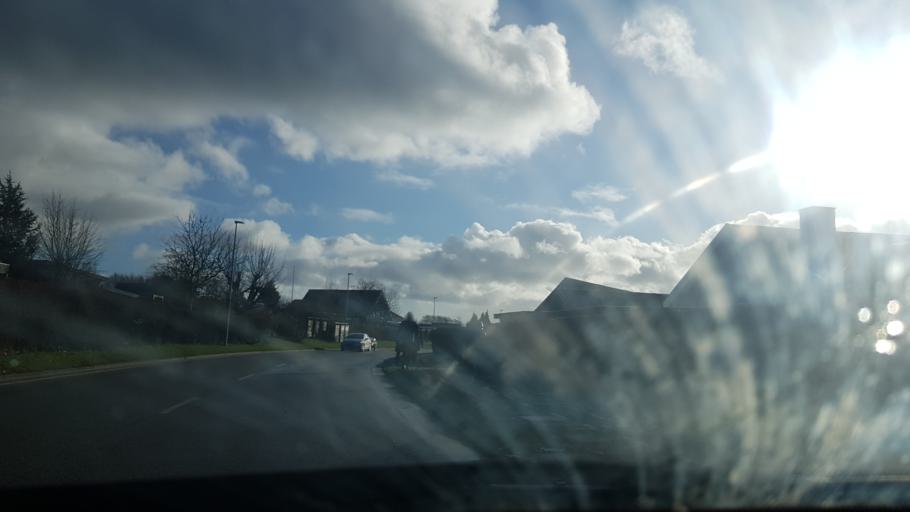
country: DK
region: South Denmark
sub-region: Fredericia Kommune
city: Taulov
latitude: 55.5183
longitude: 9.6378
